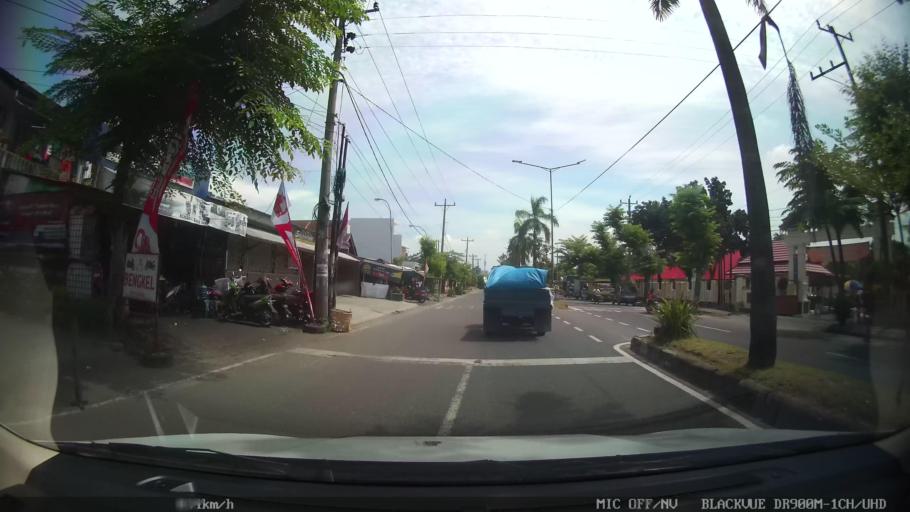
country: ID
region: North Sumatra
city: Medan
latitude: 3.5874
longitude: 98.6422
